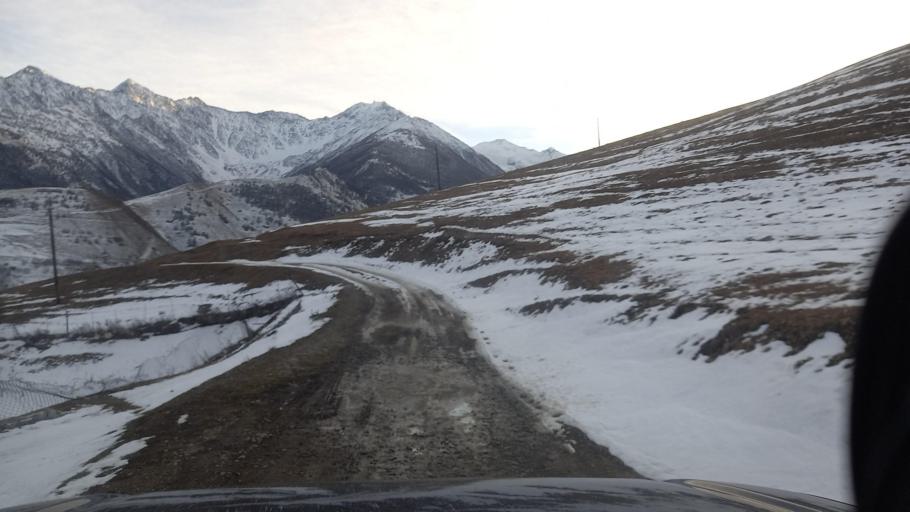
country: RU
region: Ingushetiya
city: Dzhayrakh
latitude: 42.8493
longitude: 44.5128
